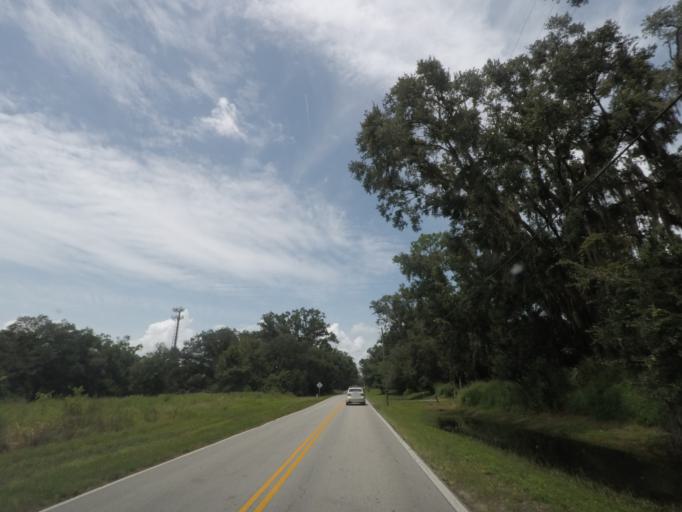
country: US
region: Florida
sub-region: Osceola County
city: Kissimmee
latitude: 28.3120
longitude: -81.4597
